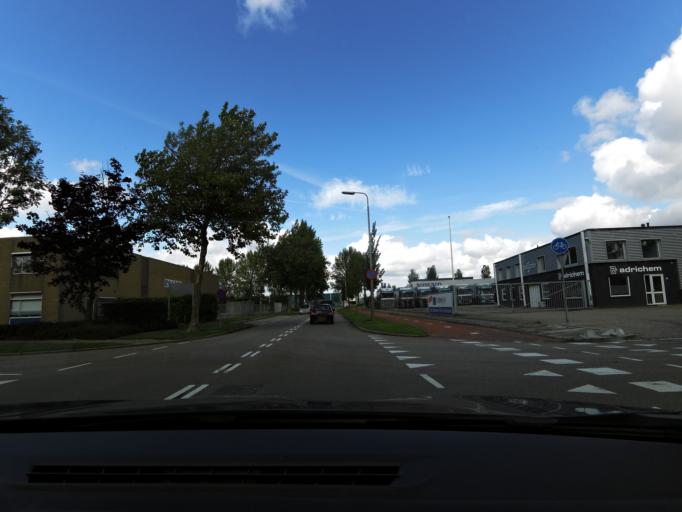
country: NL
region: South Holland
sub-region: Gemeente Oud-Beijerland
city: Oud-Beijerland
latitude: 51.8250
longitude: 4.4304
